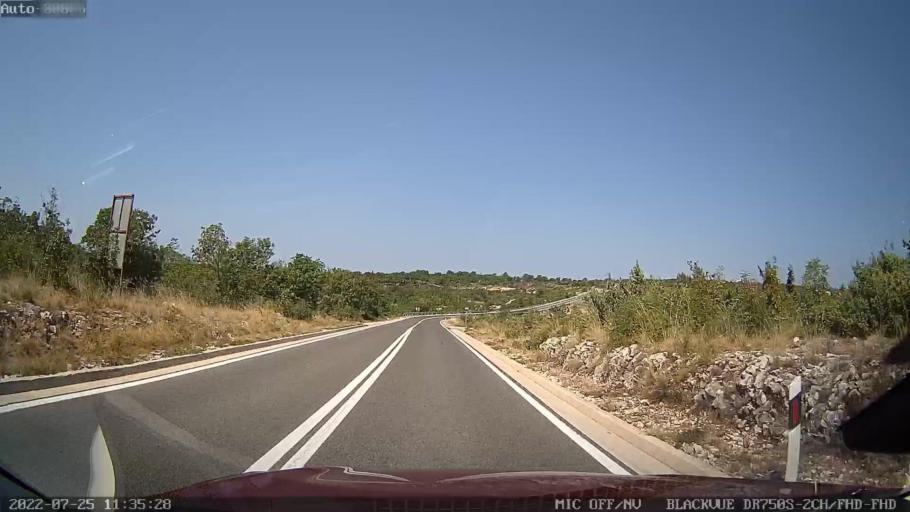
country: HR
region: Zadarska
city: Policnik
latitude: 44.2337
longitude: 15.4082
